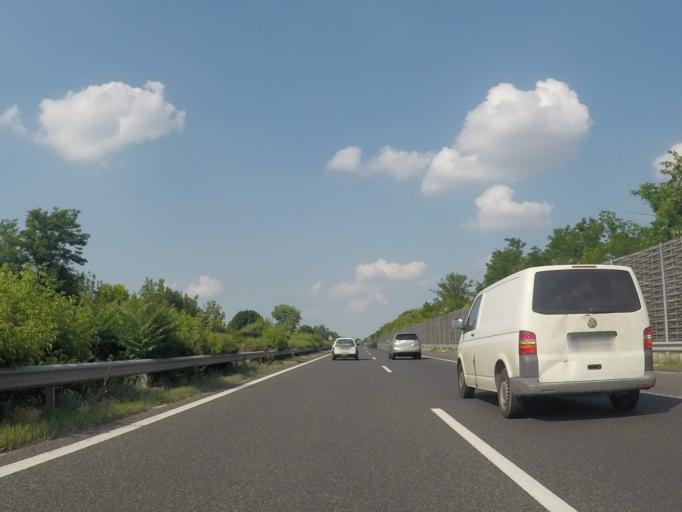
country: HU
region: Somogy
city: Balatonszabadi
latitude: 46.9630
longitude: 18.1606
